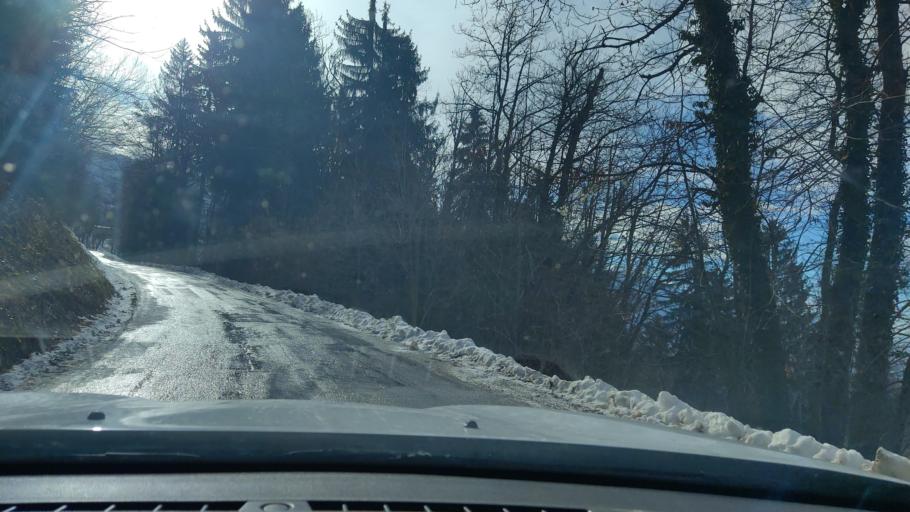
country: FR
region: Rhone-Alpes
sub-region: Departement de la Savoie
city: Marthod
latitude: 45.7029
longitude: 6.4155
